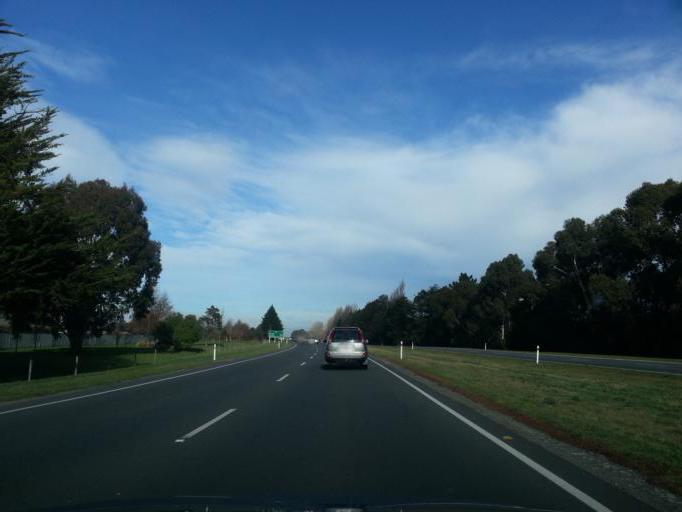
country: NZ
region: Canterbury
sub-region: Waimakariri District
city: Kaiapoi
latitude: -43.3920
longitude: 172.6402
